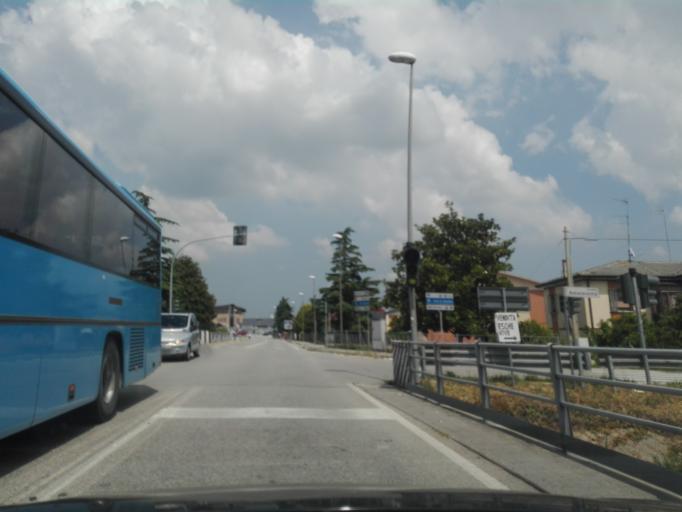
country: IT
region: Veneto
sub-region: Provincia di Rovigo
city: Adria
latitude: 45.0532
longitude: 12.0636
